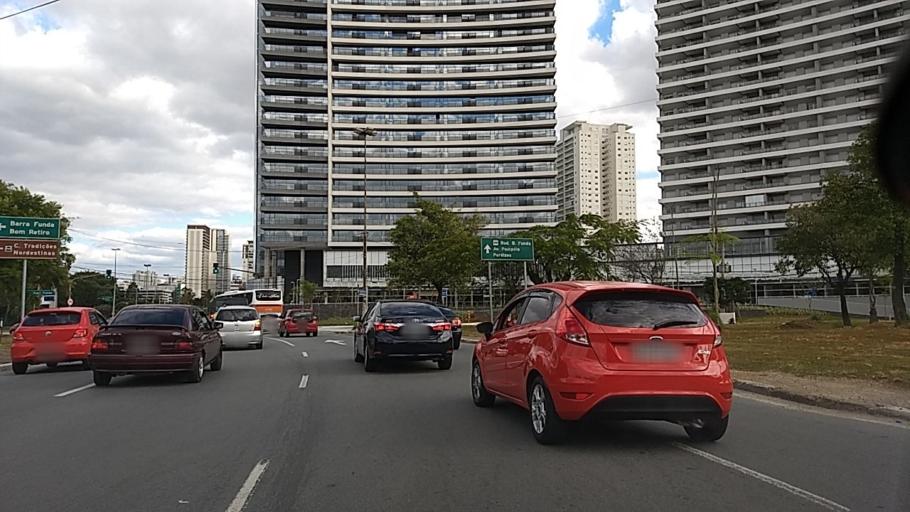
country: BR
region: Sao Paulo
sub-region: Sao Paulo
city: Sao Paulo
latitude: -23.5178
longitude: -46.6794
